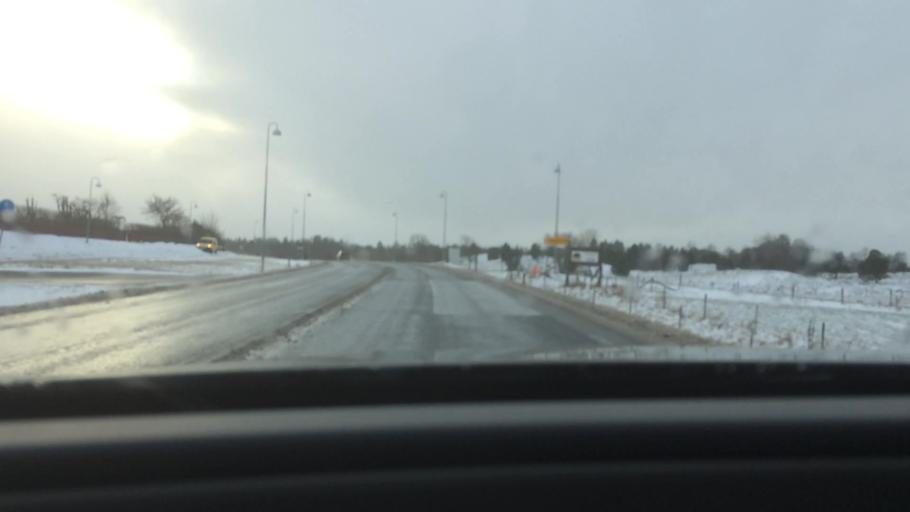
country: SE
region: Vaestra Goetaland
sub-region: Falkopings Kommun
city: Falkoeping
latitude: 57.9804
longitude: 13.5280
